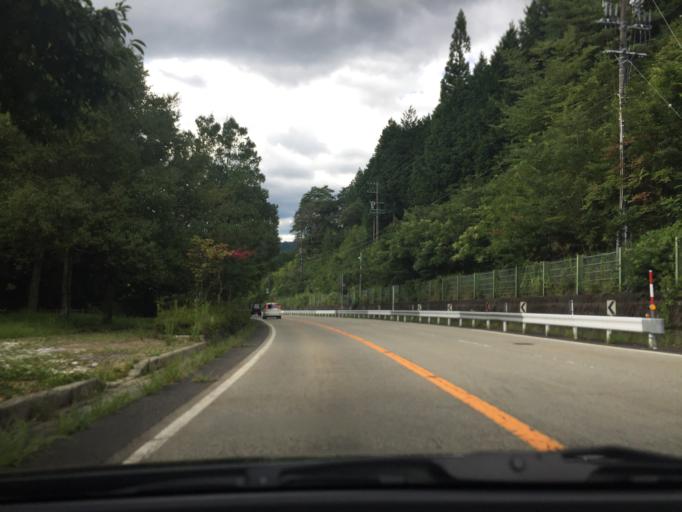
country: JP
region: Gifu
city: Nakatsugawa
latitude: 35.7567
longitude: 137.3273
